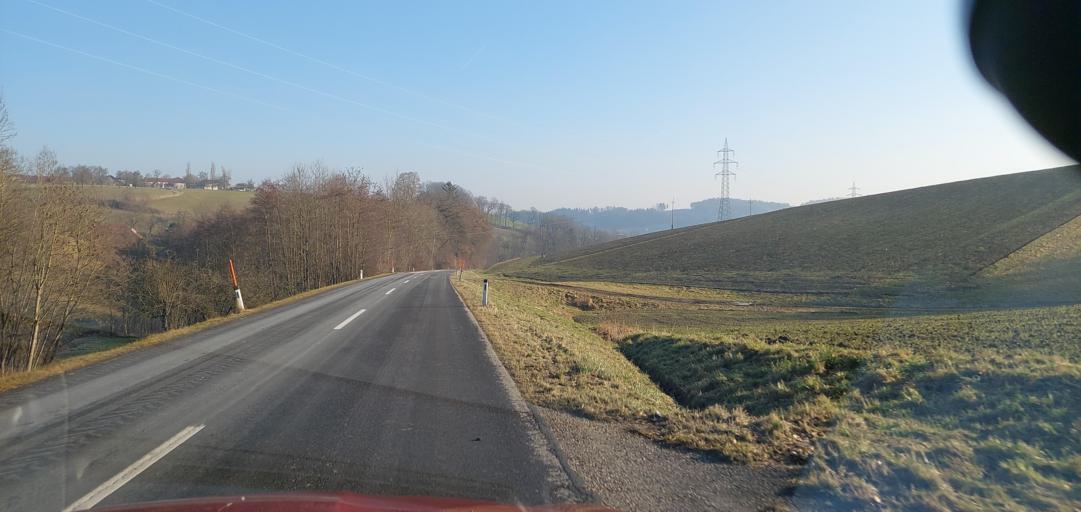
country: AT
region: Upper Austria
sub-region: Wels-Land
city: Offenhausen
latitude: 48.1867
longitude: 13.8488
